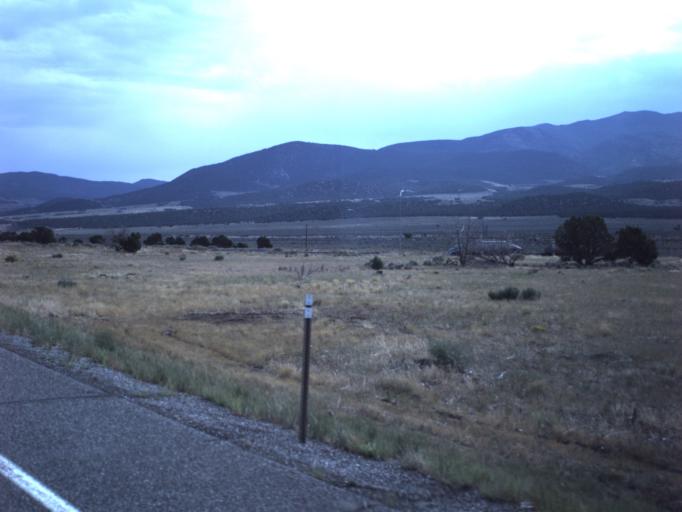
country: US
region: Utah
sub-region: Beaver County
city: Beaver
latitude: 38.5760
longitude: -112.6055
